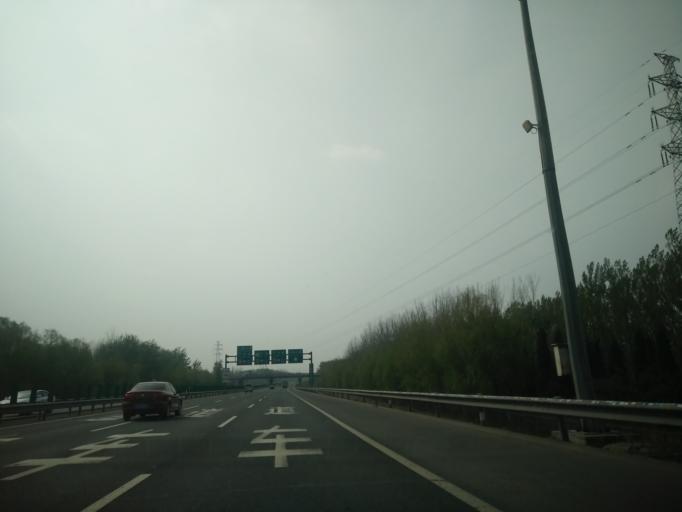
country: CN
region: Beijing
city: Taihu
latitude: 39.8409
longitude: 116.6577
